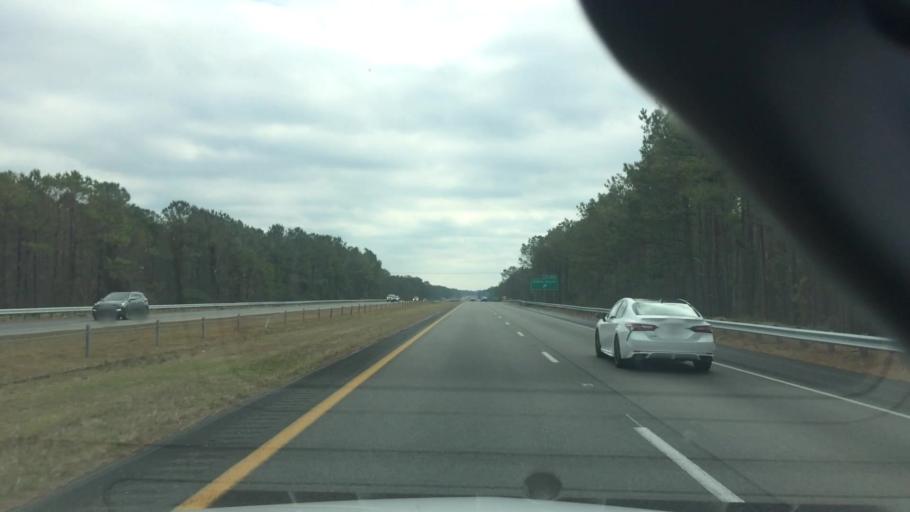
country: US
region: North Carolina
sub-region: New Hanover County
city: Castle Hayne
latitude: 34.3556
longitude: -77.8863
